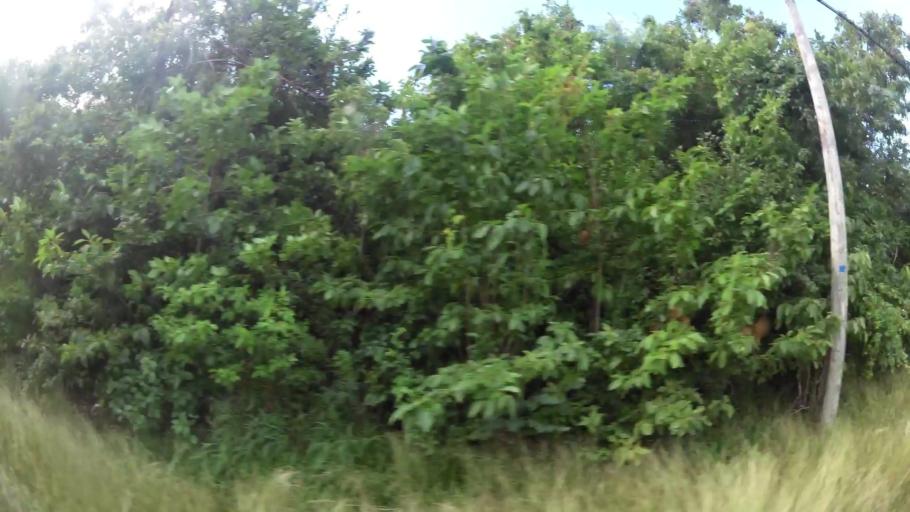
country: MQ
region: Martinique
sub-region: Martinique
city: Le Marin
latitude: 14.4273
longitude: -60.8761
